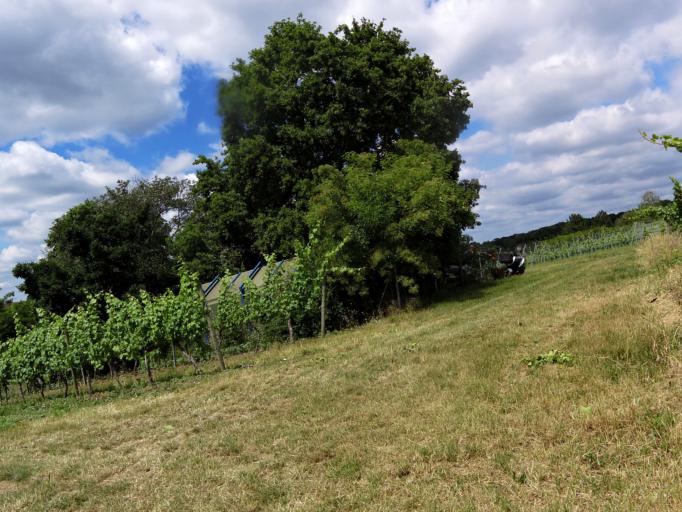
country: DE
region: Bavaria
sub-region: Regierungsbezirk Unterfranken
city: Randersacker
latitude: 49.7734
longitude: 9.9654
